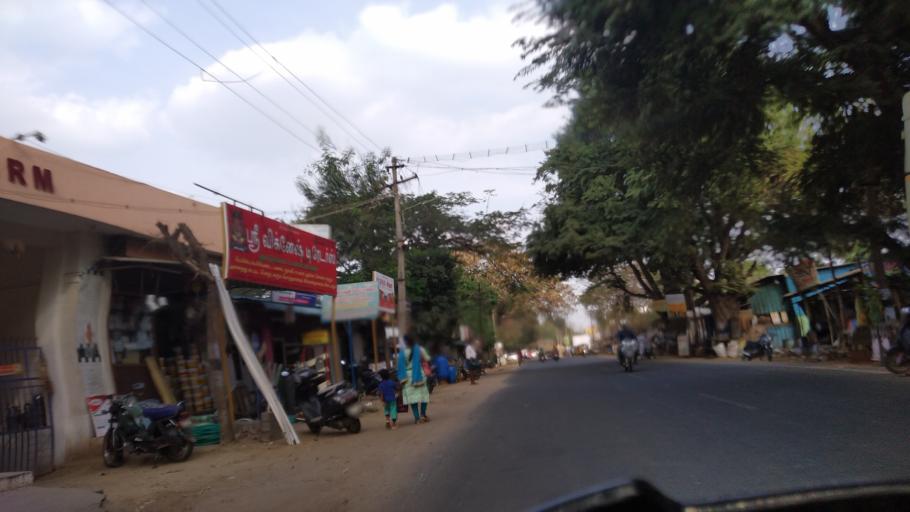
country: IN
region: Tamil Nadu
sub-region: Coimbatore
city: Perur
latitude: 10.9711
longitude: 76.8914
